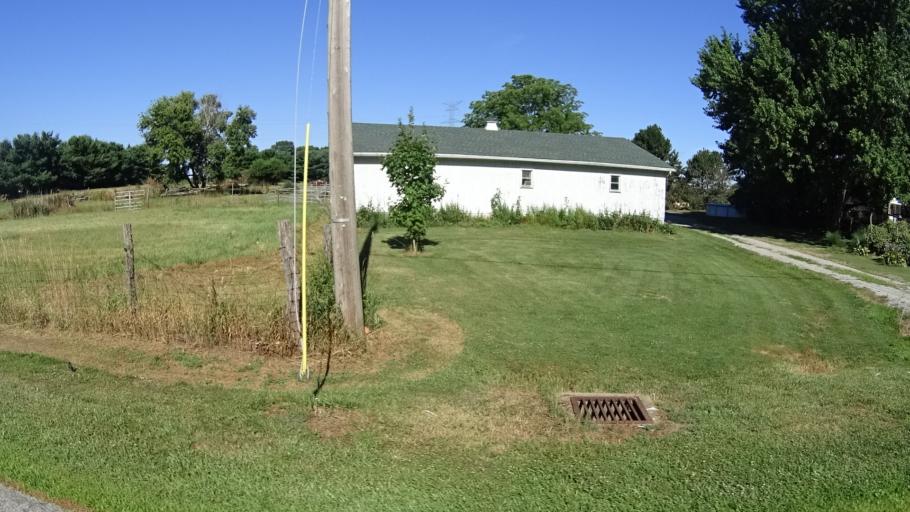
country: US
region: Ohio
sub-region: Erie County
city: Sandusky
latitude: 41.3704
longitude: -82.7254
